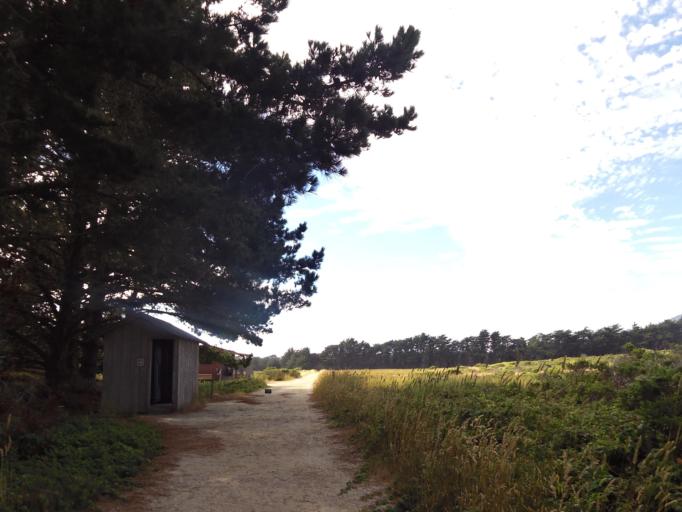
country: US
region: California
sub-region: Santa Cruz County
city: Bonny Doon
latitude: 37.1178
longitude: -122.3196
